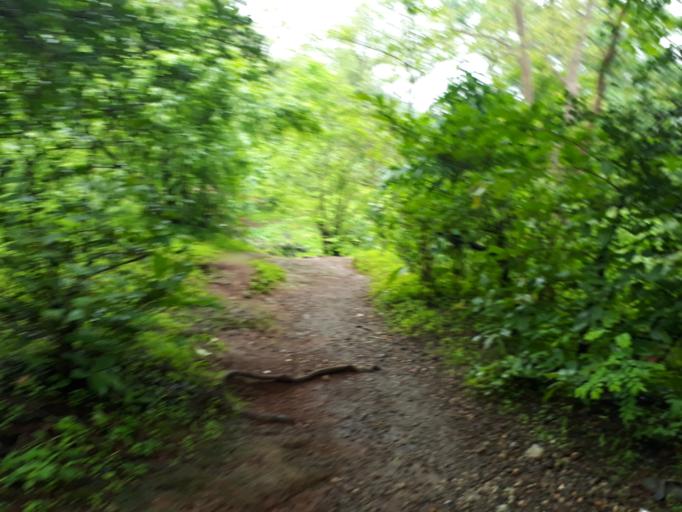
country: IN
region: Maharashtra
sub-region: Raigarh
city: Khopoli
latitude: 18.8415
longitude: 73.3814
